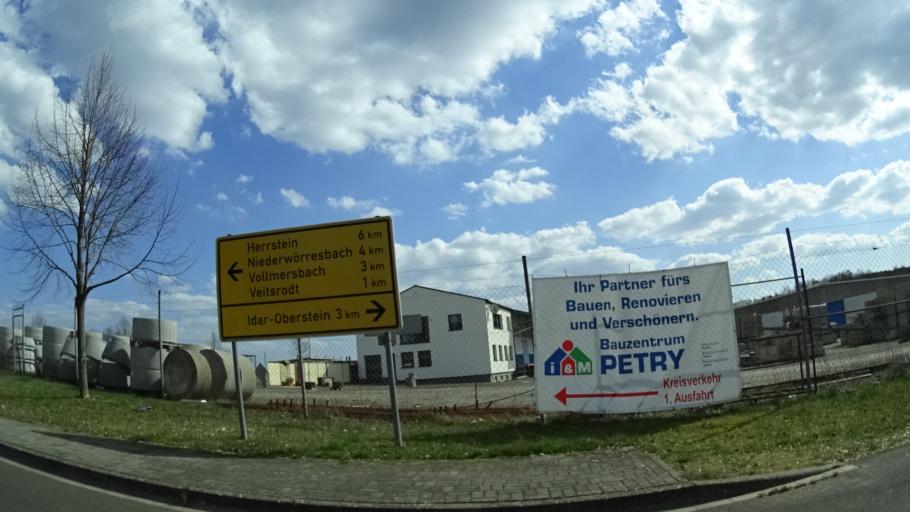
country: DE
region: Rheinland-Pfalz
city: Herborn
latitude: 49.7627
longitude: 7.2936
